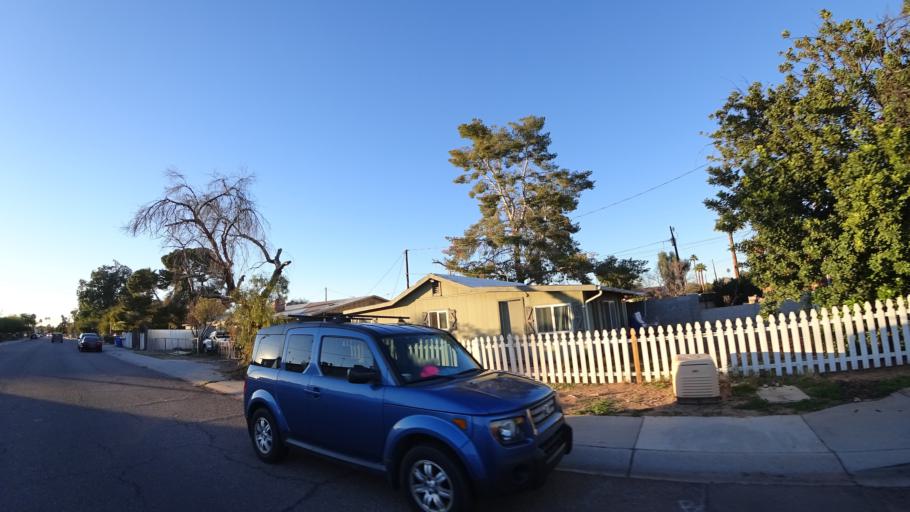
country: US
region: Arizona
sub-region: Maricopa County
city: Phoenix
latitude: 33.4823
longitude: -112.0075
